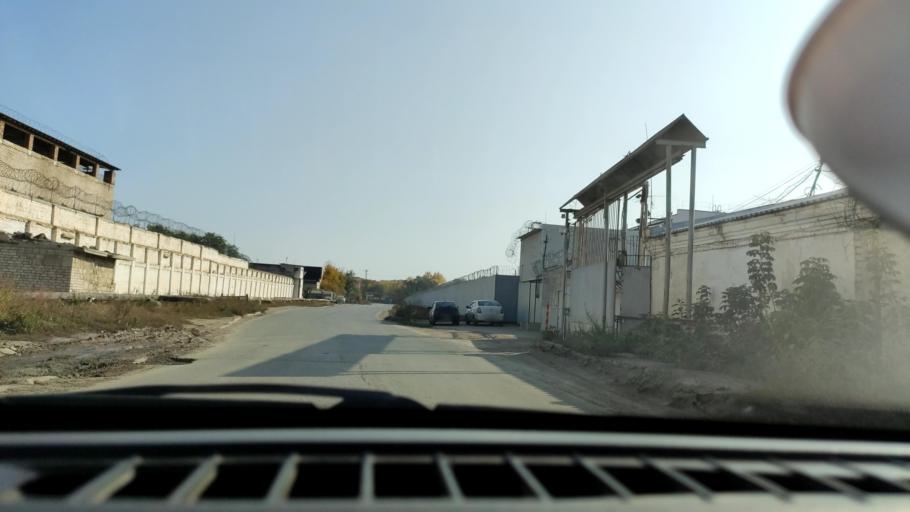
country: RU
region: Samara
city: Samara
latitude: 53.1933
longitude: 50.2630
